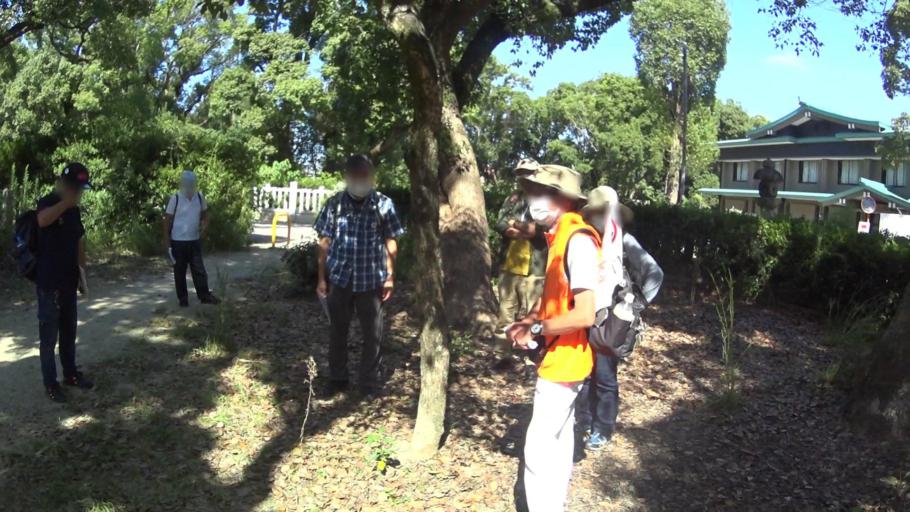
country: JP
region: Ehime
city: Kihoku-cho
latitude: 33.3963
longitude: 132.8575
